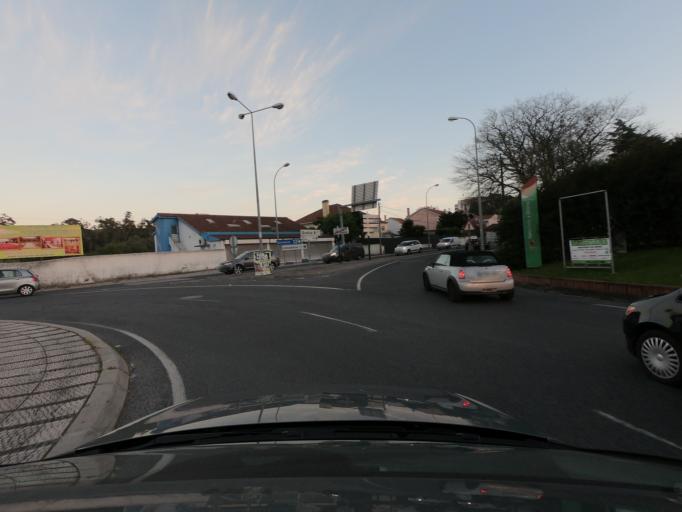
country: PT
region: Lisbon
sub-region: Sintra
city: Queluz
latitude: 38.7466
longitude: -9.2650
